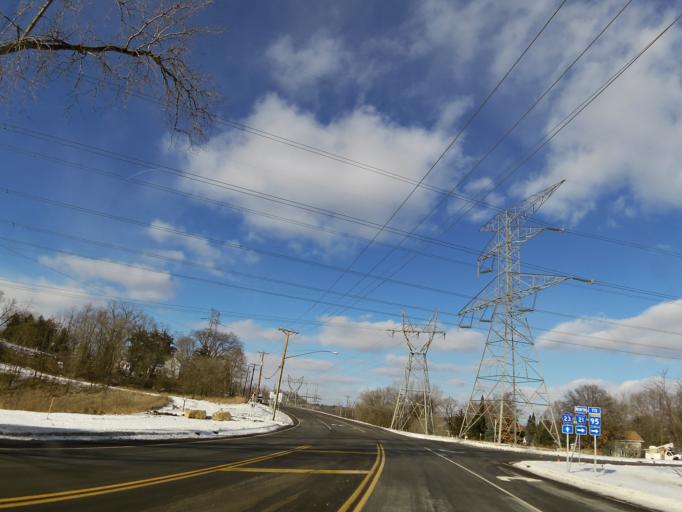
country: US
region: Minnesota
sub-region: Washington County
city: Oak Park Heights
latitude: 45.0296
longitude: -92.7912
